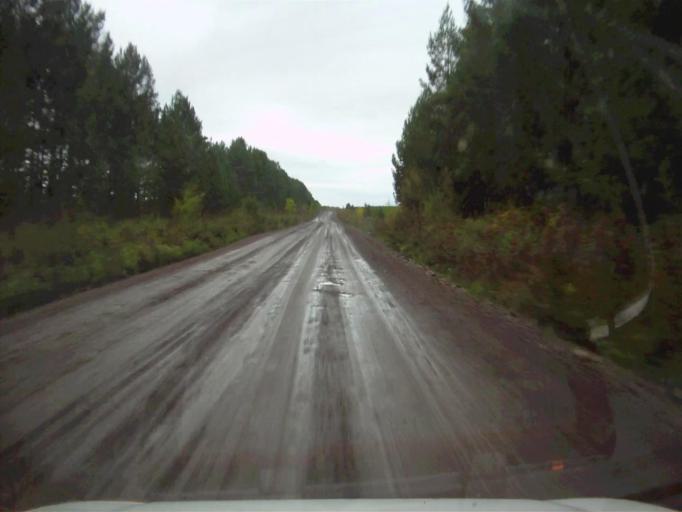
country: RU
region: Chelyabinsk
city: Nyazepetrovsk
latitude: 56.1431
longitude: 59.2878
